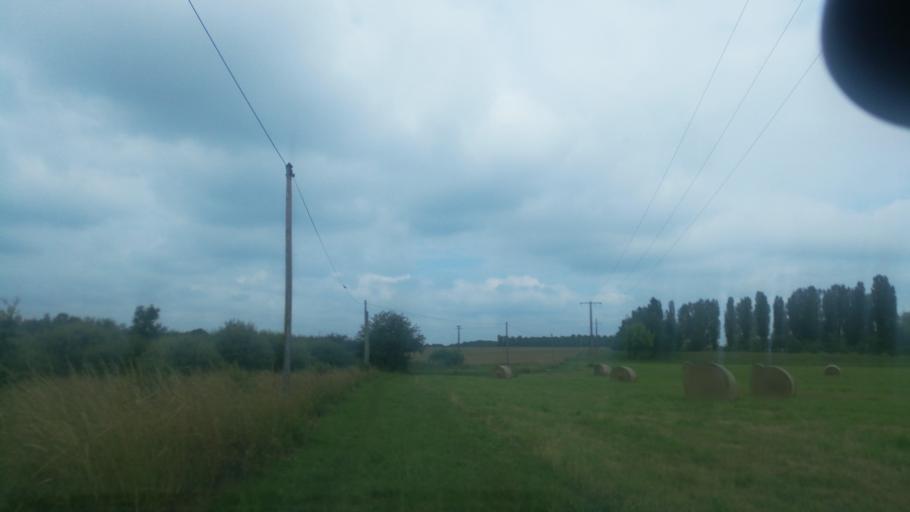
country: FR
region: Centre
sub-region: Departement du Loir-et-Cher
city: Saint-Romain-sur-Cher
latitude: 47.3480
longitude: 1.4093
